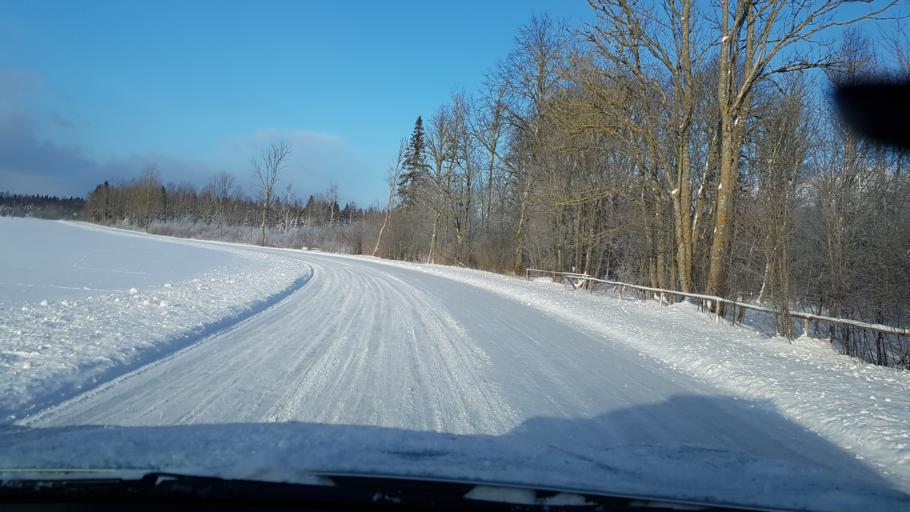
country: EE
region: Harju
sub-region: Nissi vald
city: Turba
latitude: 59.1089
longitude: 24.2284
